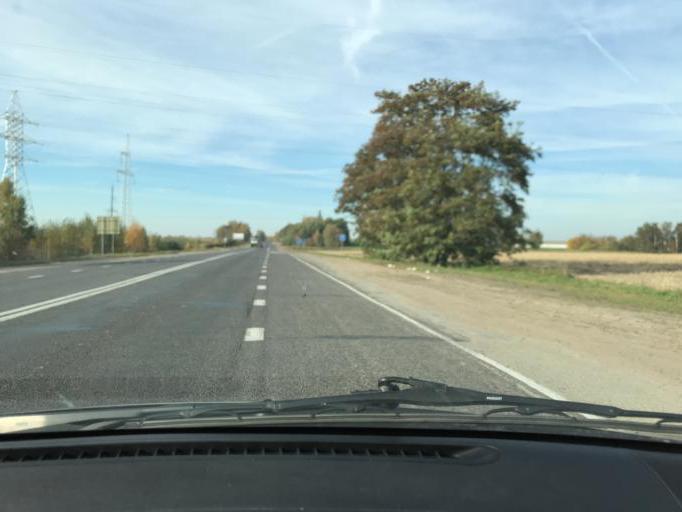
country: BY
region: Brest
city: Asnyezhytsy
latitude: 52.1874
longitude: 26.0775
